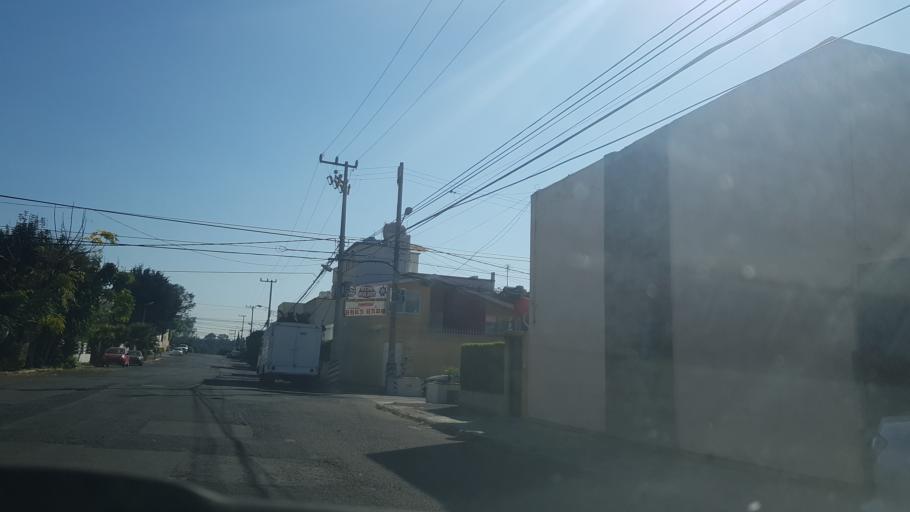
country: MX
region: Mexico
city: Naucalpan de Juarez
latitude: 19.4922
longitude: -99.2495
